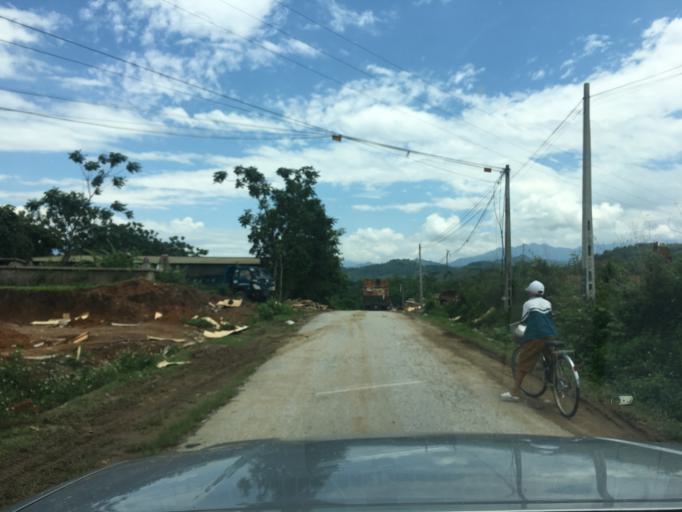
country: VN
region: Yen Bai
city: Son Thinh
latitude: 21.6583
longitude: 104.5014
